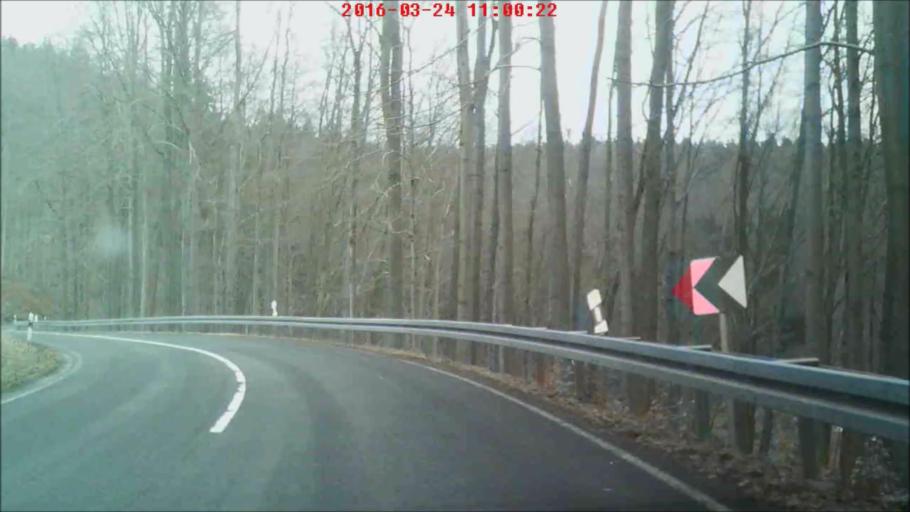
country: DE
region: Thuringia
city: Neustadt am Rennsteig
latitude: 50.5530
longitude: 10.9234
